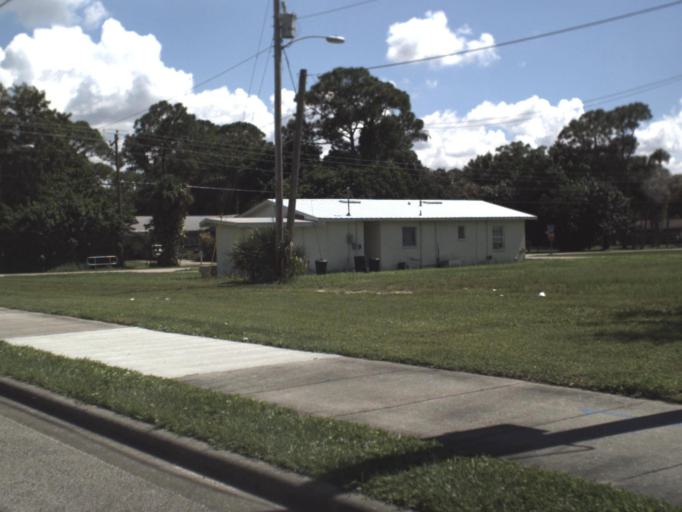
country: US
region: Florida
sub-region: Lee County
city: Palmona Park
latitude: 26.6820
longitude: -81.8899
